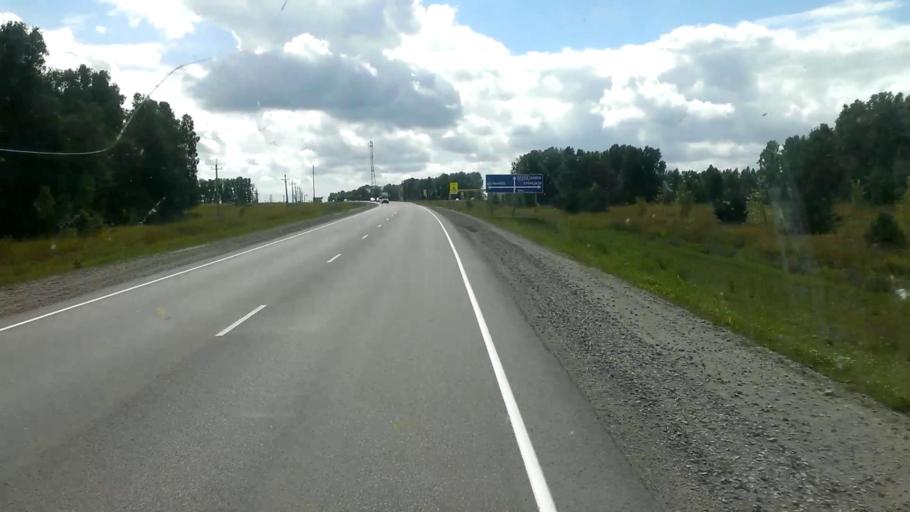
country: RU
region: Altai Krai
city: Troitskoye
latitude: 52.9719
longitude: 84.7480
